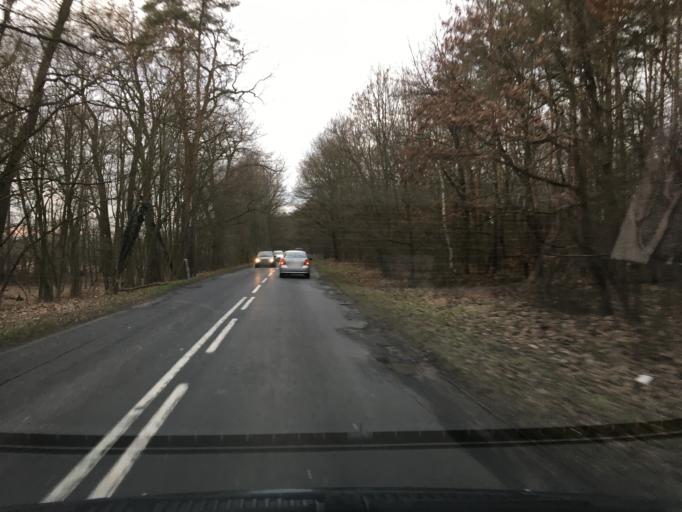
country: PL
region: Opole Voivodeship
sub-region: Powiat krapkowicki
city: Januszkowice
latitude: 50.3674
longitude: 18.1525
